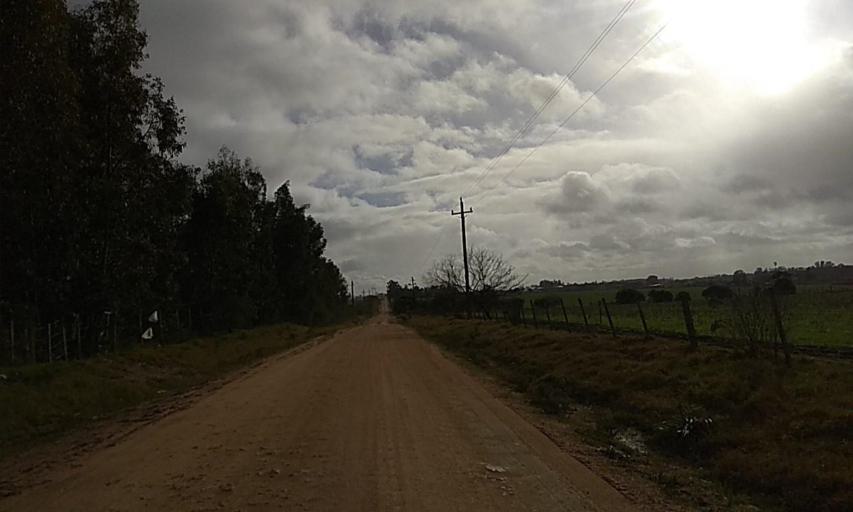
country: UY
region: Florida
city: Florida
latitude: -34.0670
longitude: -56.2311
